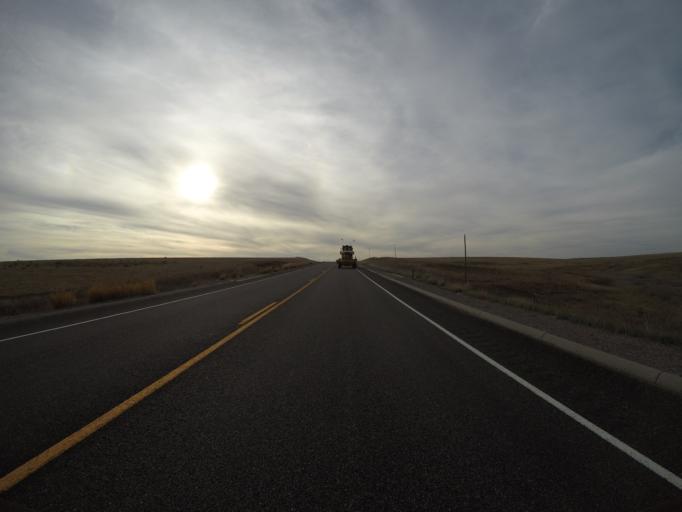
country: US
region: Kansas
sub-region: Cheyenne County
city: Saint Francis
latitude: 39.7468
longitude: -102.0718
